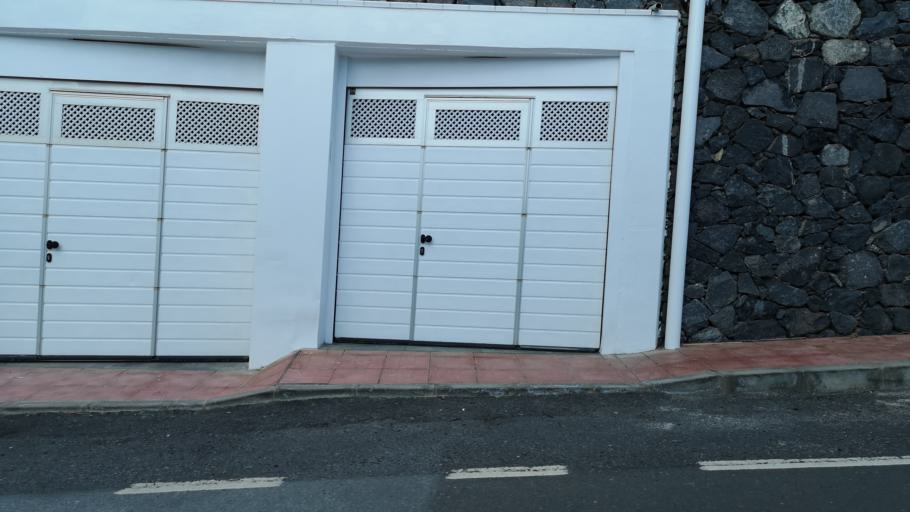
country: ES
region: Canary Islands
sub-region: Provincia de Santa Cruz de Tenerife
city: Hermigua
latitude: 28.1783
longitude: -17.1856
